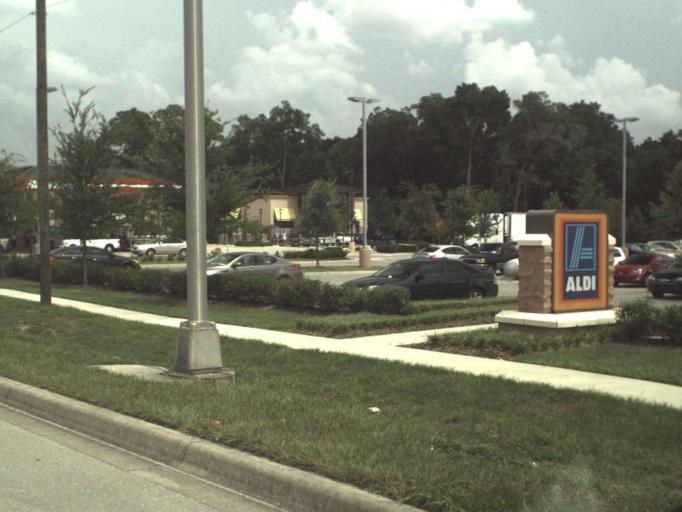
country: US
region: Florida
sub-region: Orange County
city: South Apopka
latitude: 28.6728
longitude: -81.4796
